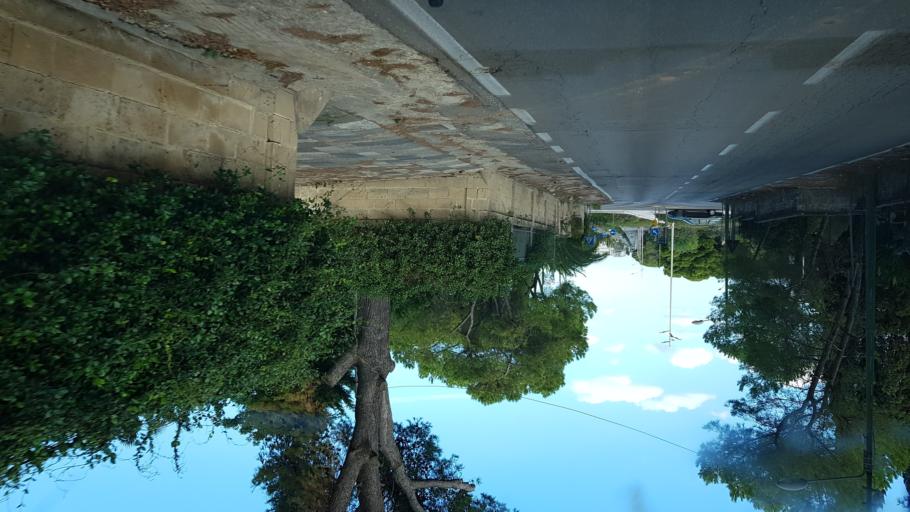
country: IT
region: Apulia
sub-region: Provincia di Lecce
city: Nardo
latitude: 40.1555
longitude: 18.0191
